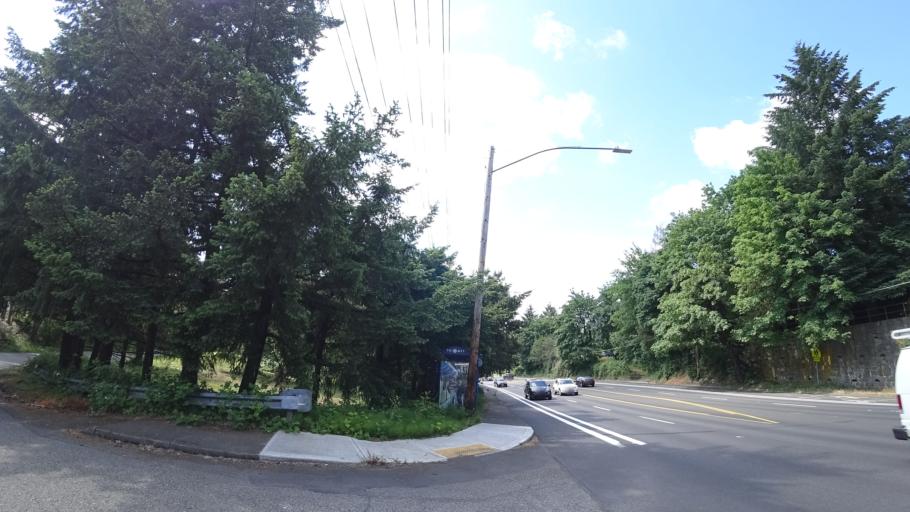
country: US
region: Oregon
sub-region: Multnomah County
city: Portland
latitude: 45.4791
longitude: -122.7007
